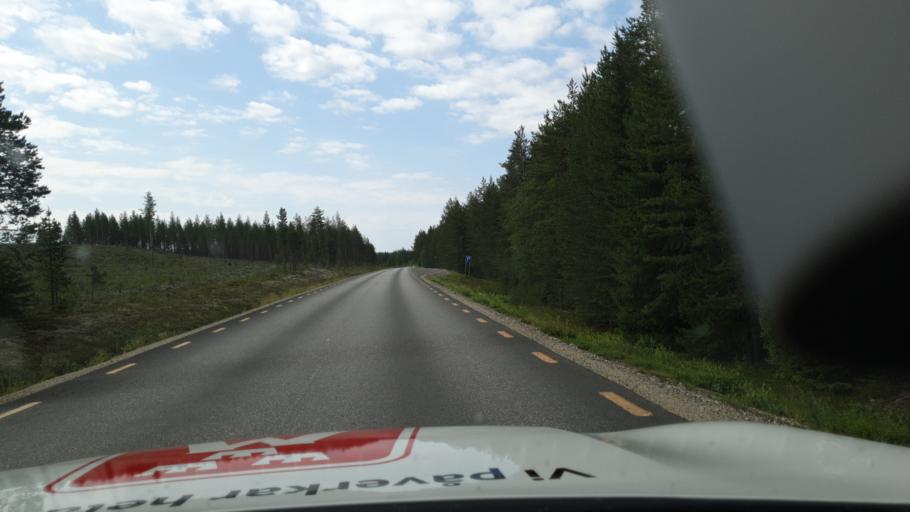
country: SE
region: Vaesterbotten
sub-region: Norsjo Kommun
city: Norsjoe
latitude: 64.5046
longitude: 19.3329
